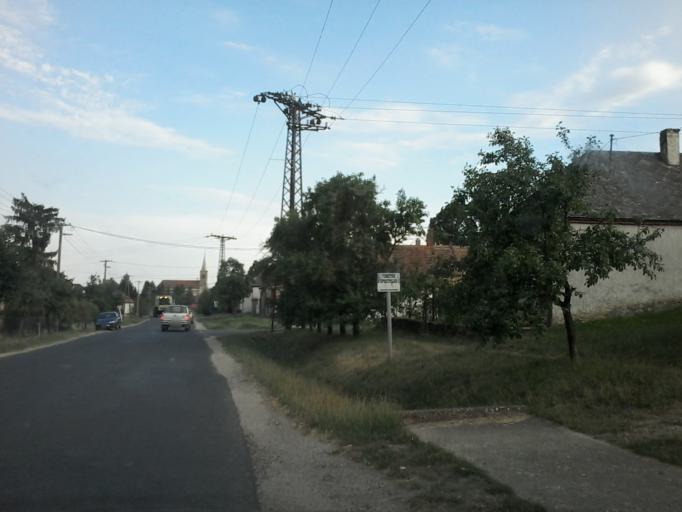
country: HU
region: Vas
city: Sarvar
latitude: 47.2123
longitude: 17.0186
